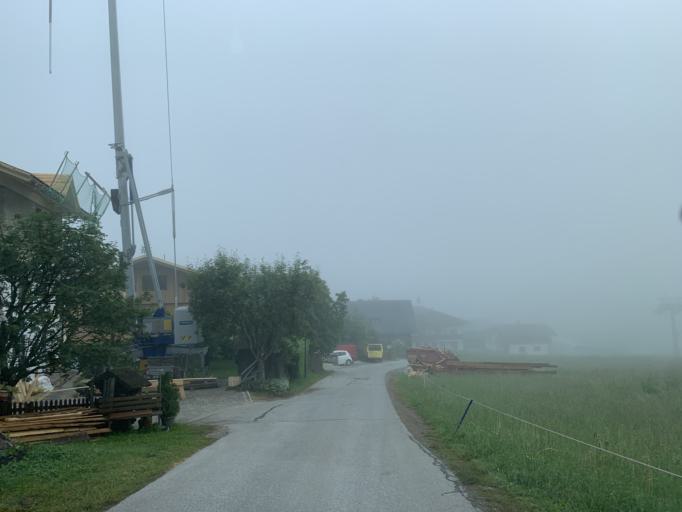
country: AT
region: Salzburg
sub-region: Politischer Bezirk Sankt Johann im Pongau
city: Forstau
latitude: 47.3868
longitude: 13.5962
